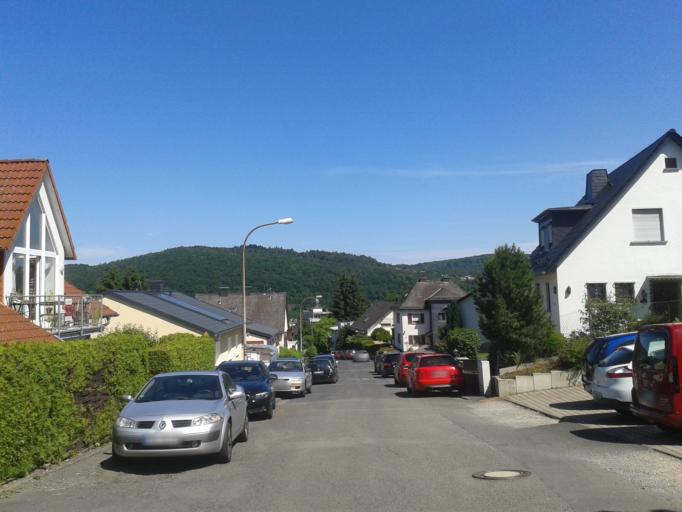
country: DE
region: Hesse
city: Herborn
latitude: 50.6838
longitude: 8.2927
